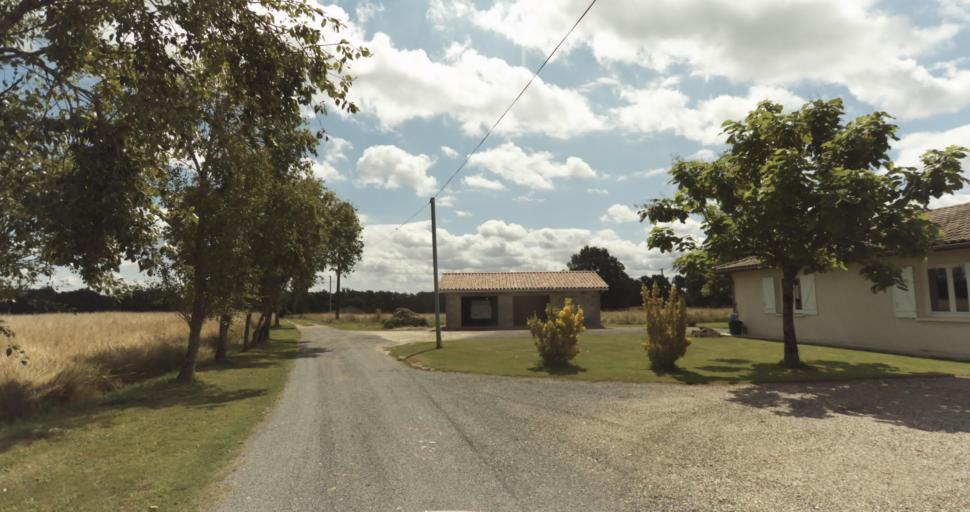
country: FR
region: Aquitaine
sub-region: Departement de la Gironde
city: Bazas
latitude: 44.4644
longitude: -0.1828
